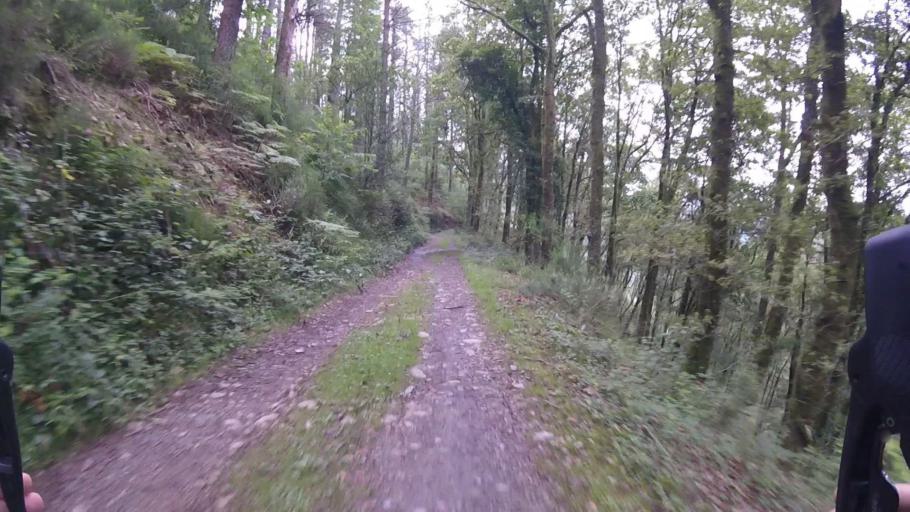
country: ES
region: Navarre
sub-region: Provincia de Navarra
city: Arano
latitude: 43.2509
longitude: -1.8659
